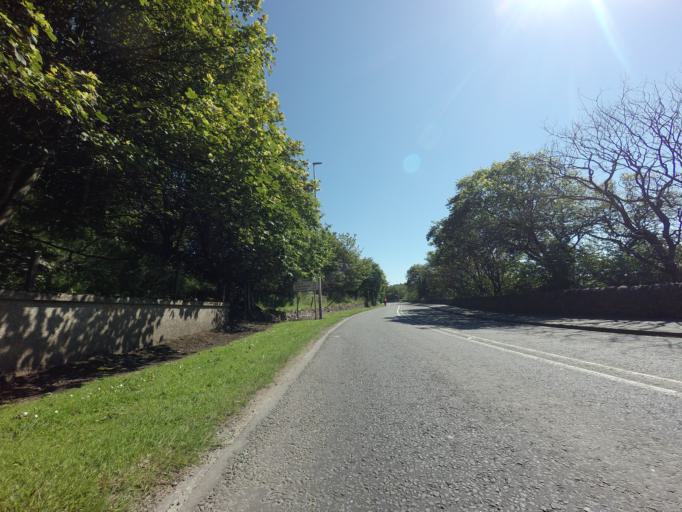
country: GB
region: Scotland
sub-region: Aberdeenshire
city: Macduff
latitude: 57.6611
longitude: -2.5115
